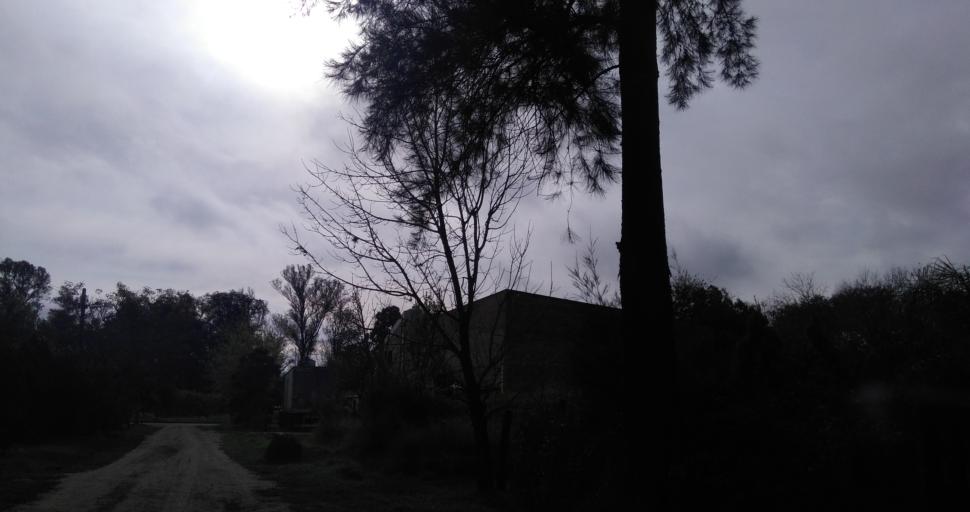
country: AR
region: Chaco
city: Colonia Benitez
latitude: -27.3245
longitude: -58.9572
